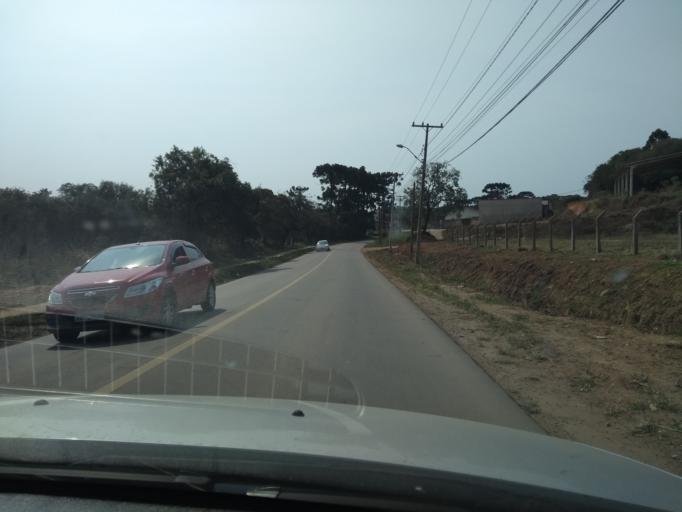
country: BR
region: Parana
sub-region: Araucaria
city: Araucaria
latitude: -25.6124
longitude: -49.3396
